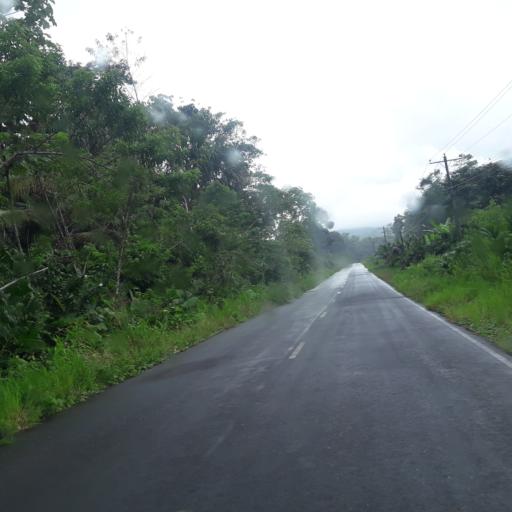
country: EC
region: Napo
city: Tena
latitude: -1.0436
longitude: -77.6638
